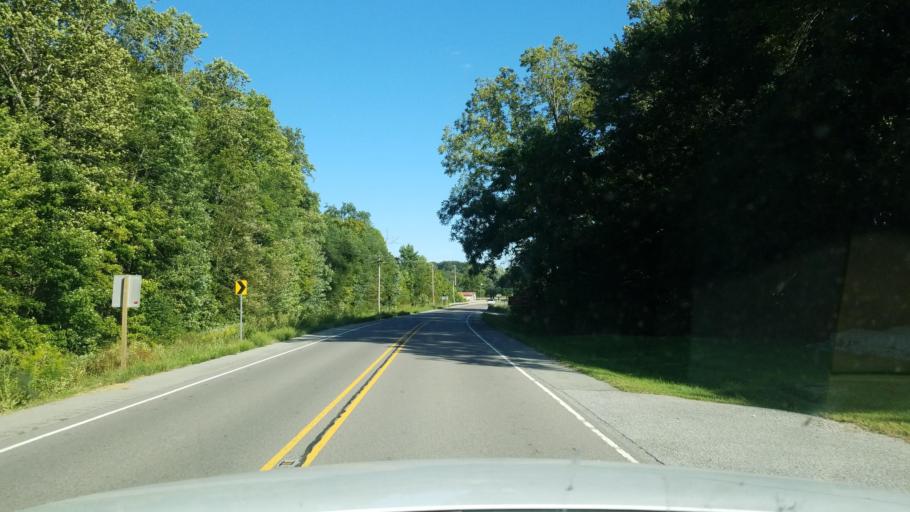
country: US
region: Illinois
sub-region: Hardin County
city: Rosiclare
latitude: 37.5817
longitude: -88.4388
